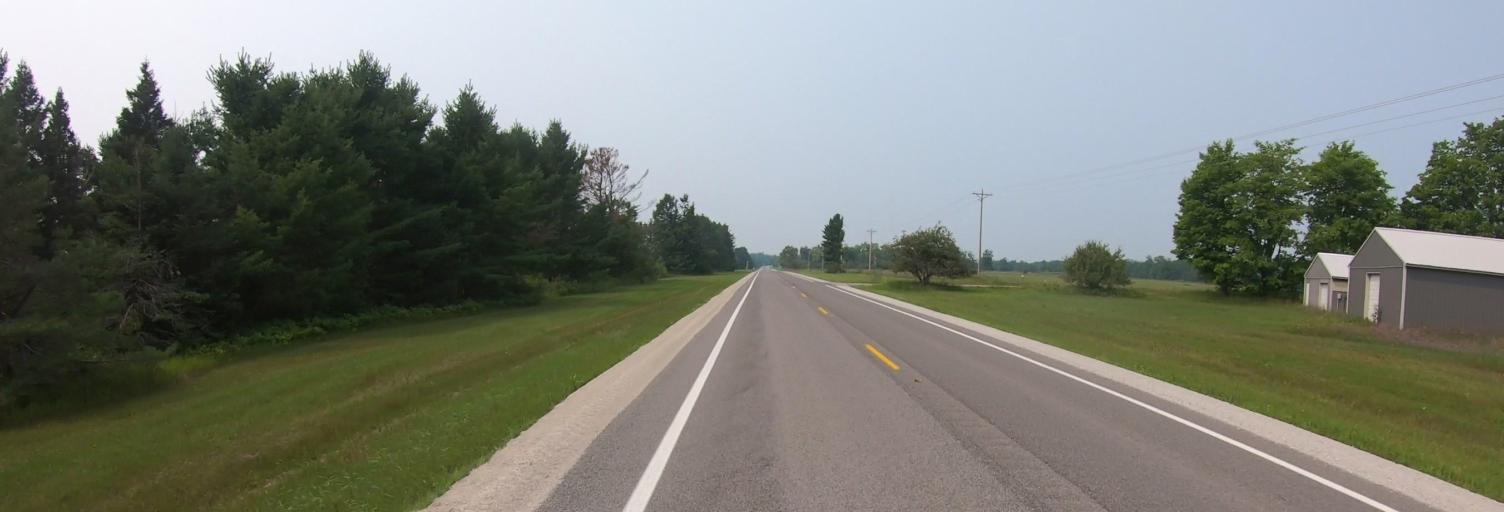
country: US
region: Michigan
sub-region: Chippewa County
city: Sault Ste. Marie
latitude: 46.0321
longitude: -84.0840
